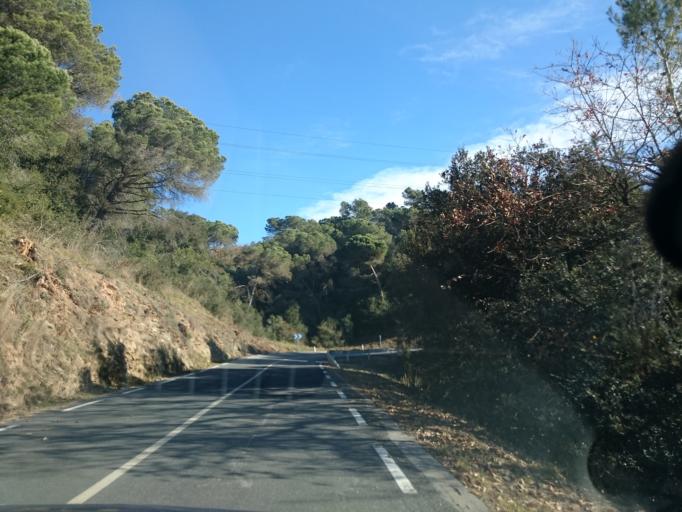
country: ES
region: Catalonia
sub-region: Provincia de Barcelona
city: Molins de Rei
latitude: 41.4286
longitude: 2.0441
